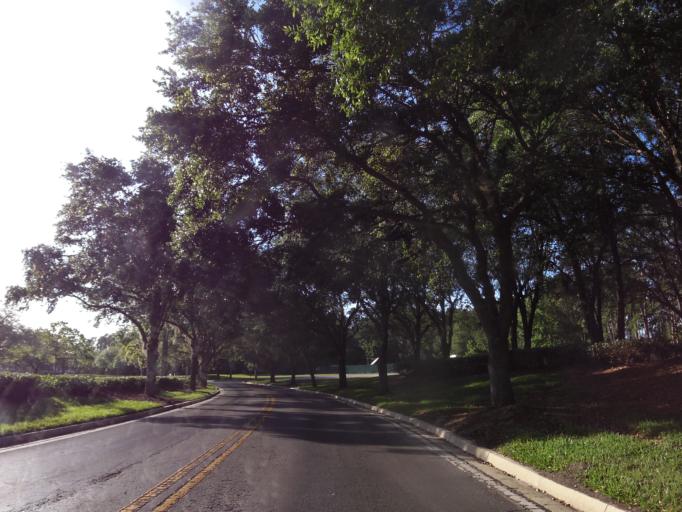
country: US
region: Florida
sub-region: Saint Johns County
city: Villano Beach
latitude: 29.9934
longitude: -81.4670
